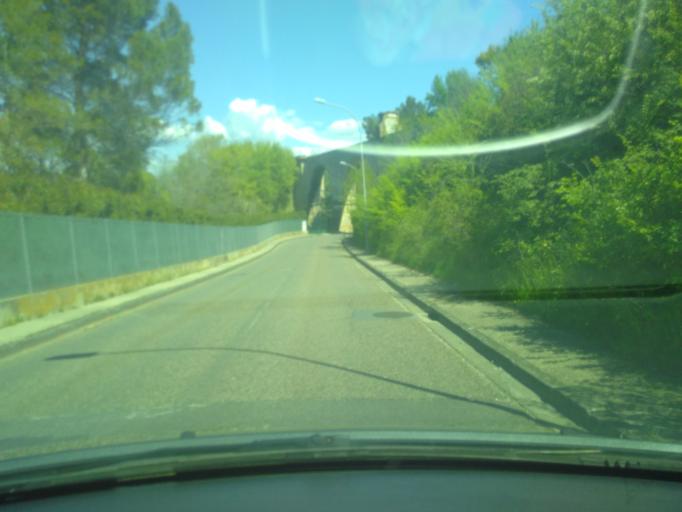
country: FR
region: Provence-Alpes-Cote d'Azur
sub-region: Departement du Vaucluse
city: Carpentras
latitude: 44.0594
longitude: 5.0566
